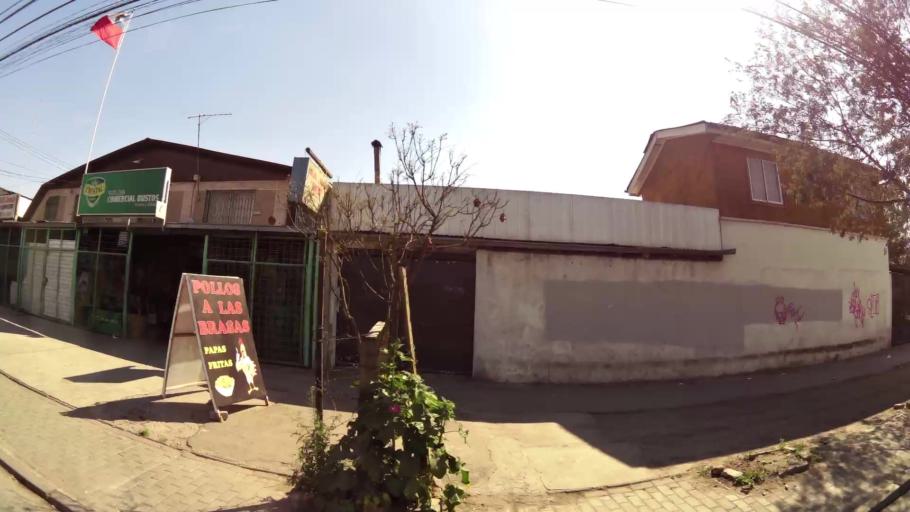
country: CL
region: Santiago Metropolitan
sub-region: Provincia de Santiago
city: La Pintana
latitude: -33.5398
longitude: -70.6036
